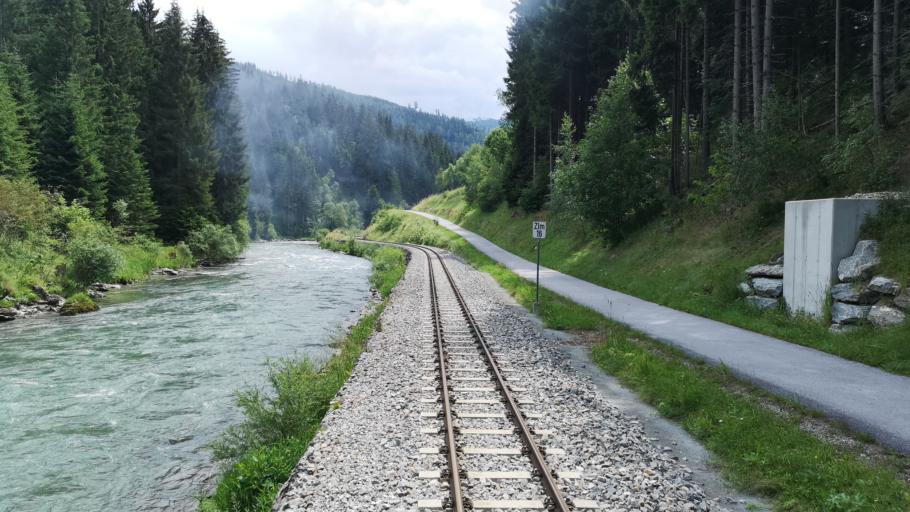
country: AT
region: Salzburg
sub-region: Politischer Bezirk Tamsweg
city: Tamsweg
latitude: 47.0975
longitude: 13.8208
